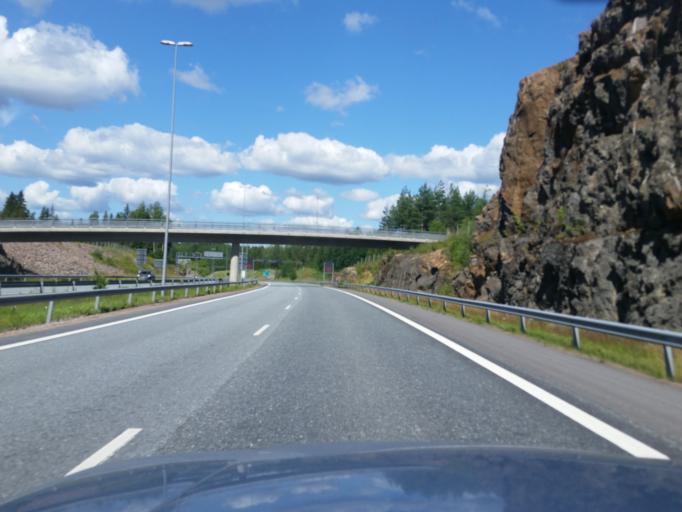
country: FI
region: Uusimaa
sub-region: Helsinki
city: Saukkola
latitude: 60.3206
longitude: 23.9648
